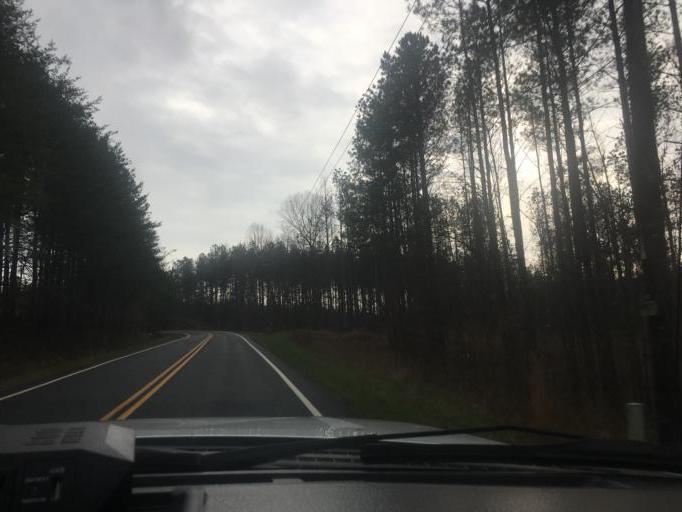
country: US
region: Georgia
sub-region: Dawson County
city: Dawsonville
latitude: 34.3473
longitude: -84.2062
